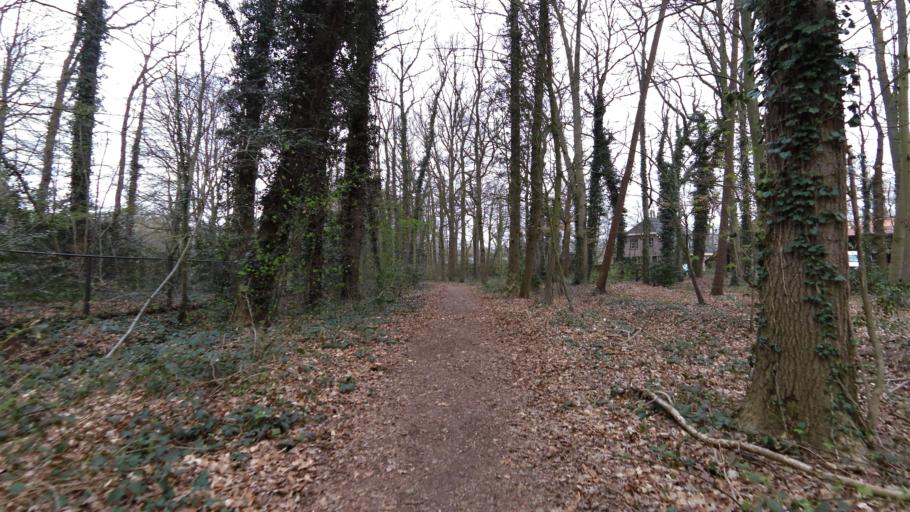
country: NL
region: Gelderland
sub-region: Gemeente Barneveld
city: Zwartebroek
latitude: 52.2052
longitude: 5.5133
